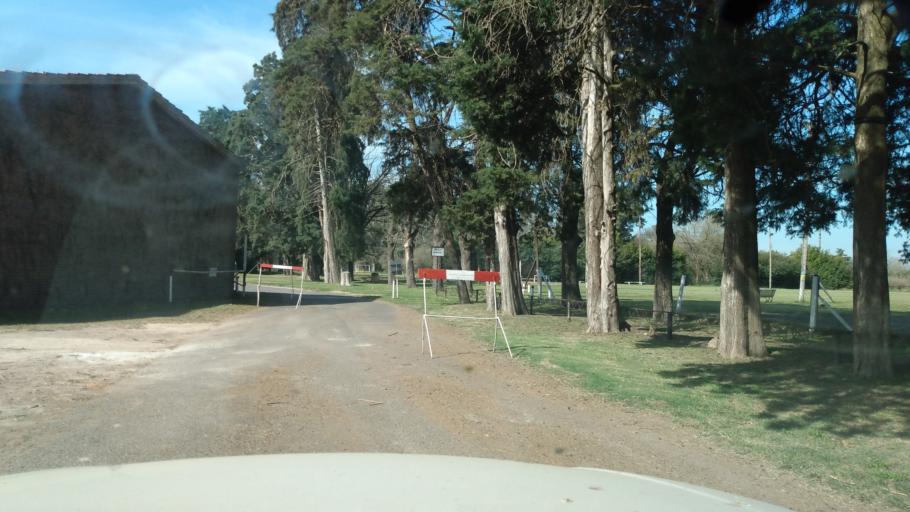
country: AR
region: Buenos Aires
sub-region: Partido de Lujan
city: Lujan
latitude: -34.5937
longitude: -59.1856
